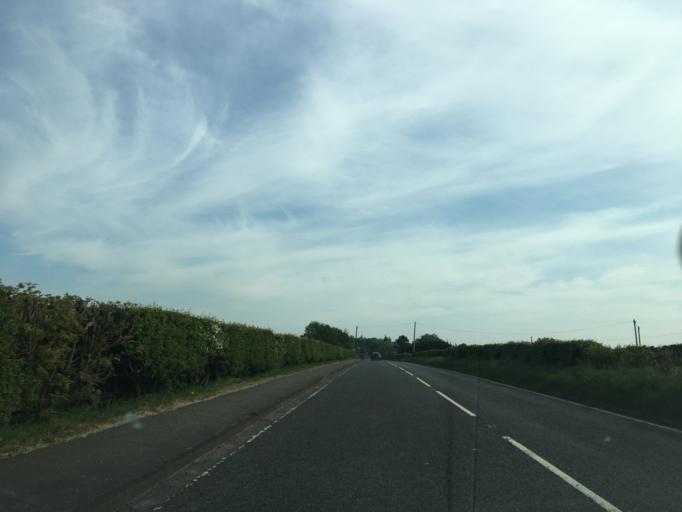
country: GB
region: Scotland
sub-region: Midlothian
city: Loanhead
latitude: 55.8772
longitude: -3.1926
